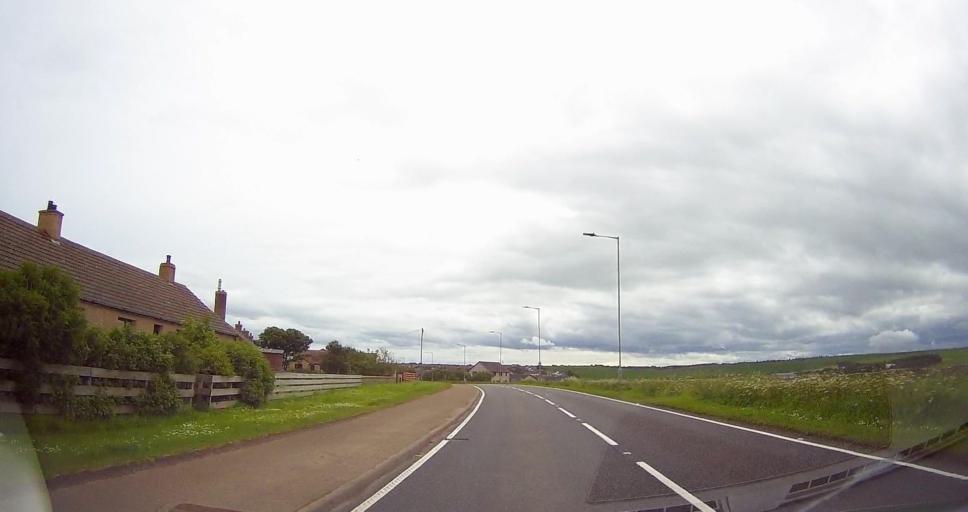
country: GB
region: Scotland
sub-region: Highland
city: Thurso
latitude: 58.6047
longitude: -3.5508
